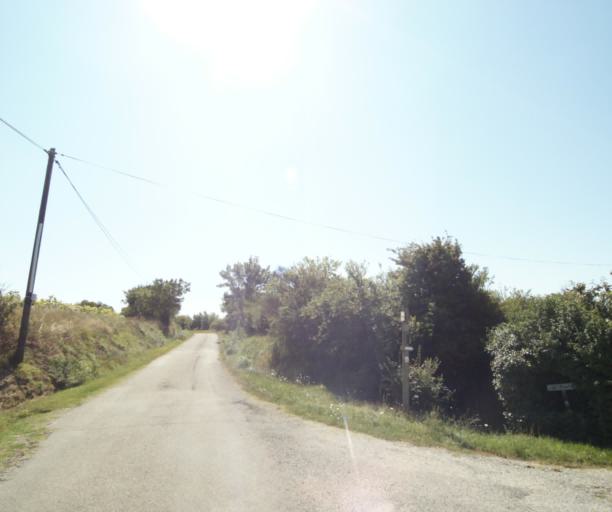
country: FR
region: Midi-Pyrenees
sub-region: Departement de l'Ariege
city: Lezat-sur-Leze
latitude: 43.2576
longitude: 1.3936
